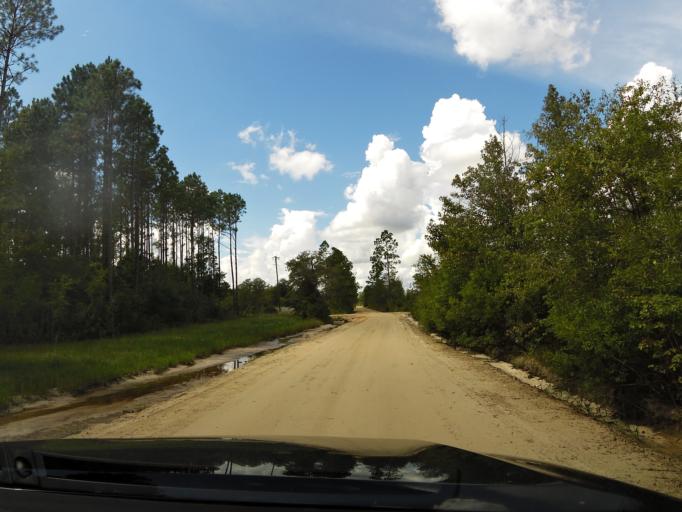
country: US
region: Georgia
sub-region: Brantley County
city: Nahunta
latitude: 31.0915
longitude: -82.0206
